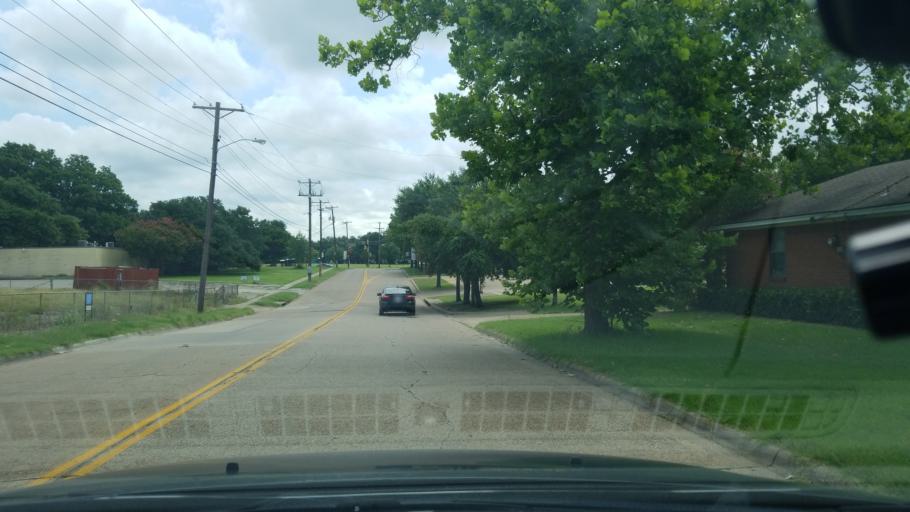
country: US
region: Texas
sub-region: Dallas County
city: Garland
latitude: 32.8265
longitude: -96.6788
